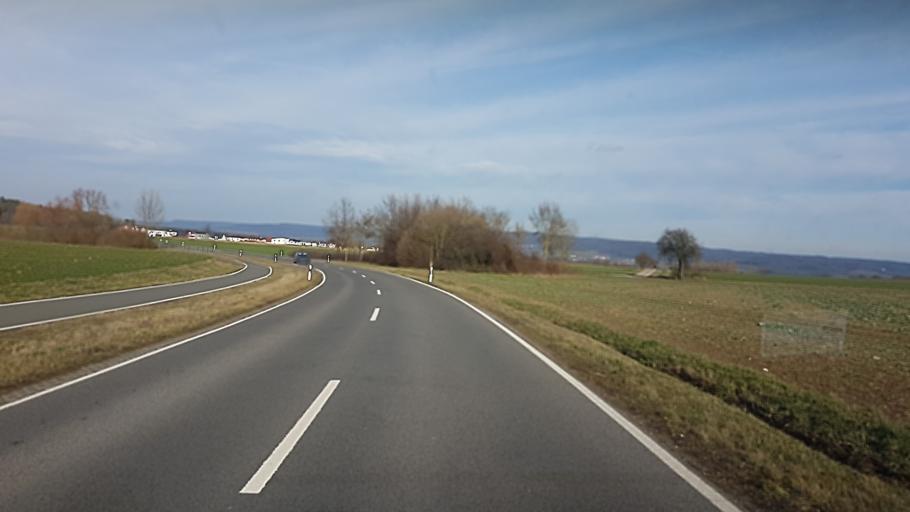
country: DE
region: Bavaria
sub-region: Upper Franconia
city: Hallerndorf
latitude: 49.7917
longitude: 10.9640
